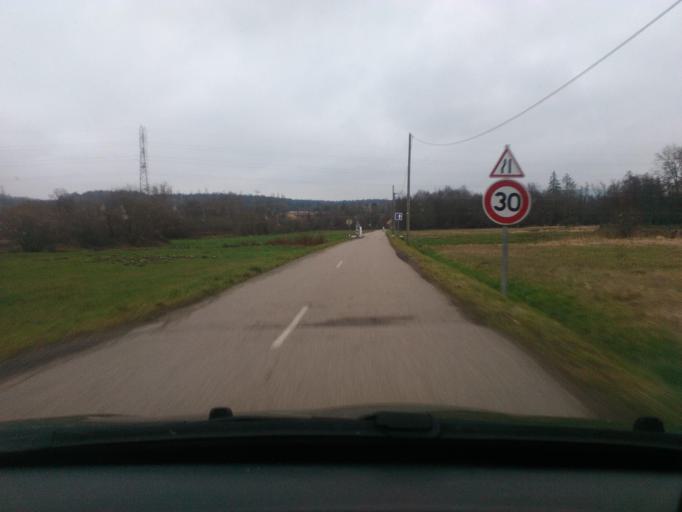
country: FR
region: Lorraine
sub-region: Departement des Vosges
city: Etival-Clairefontaine
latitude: 48.3577
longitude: 6.8710
